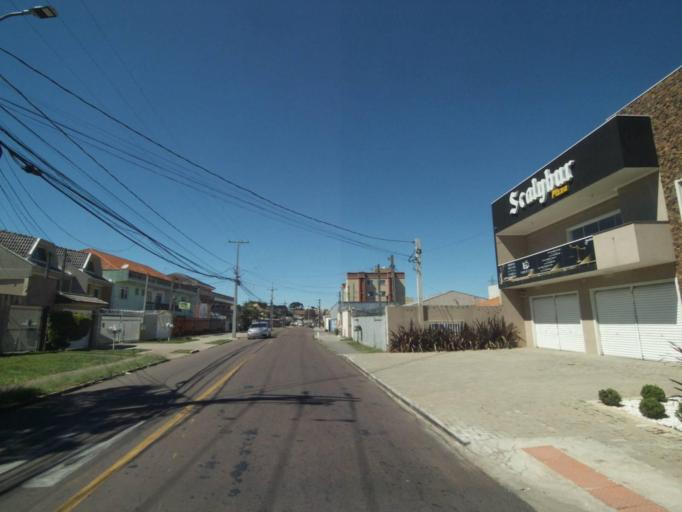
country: BR
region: Parana
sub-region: Curitiba
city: Curitiba
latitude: -25.4817
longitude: -49.3400
